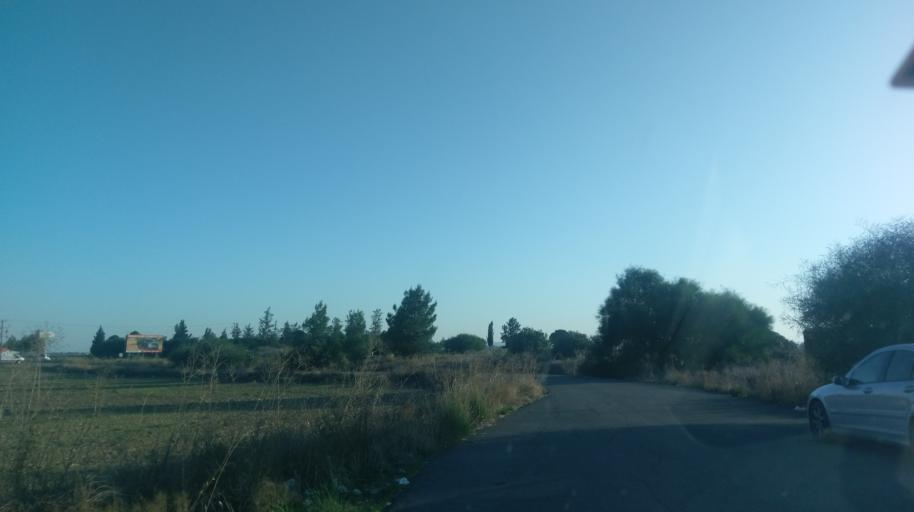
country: CY
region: Ammochostos
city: Lefkonoiko
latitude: 35.1956
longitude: 33.6188
